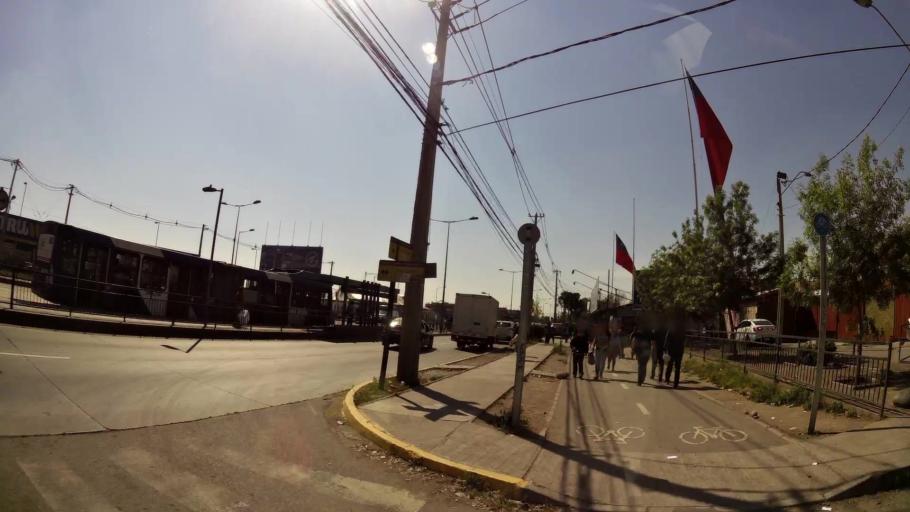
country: CL
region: Santiago Metropolitan
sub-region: Provincia de Santiago
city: La Pintana
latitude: -33.5653
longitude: -70.6301
